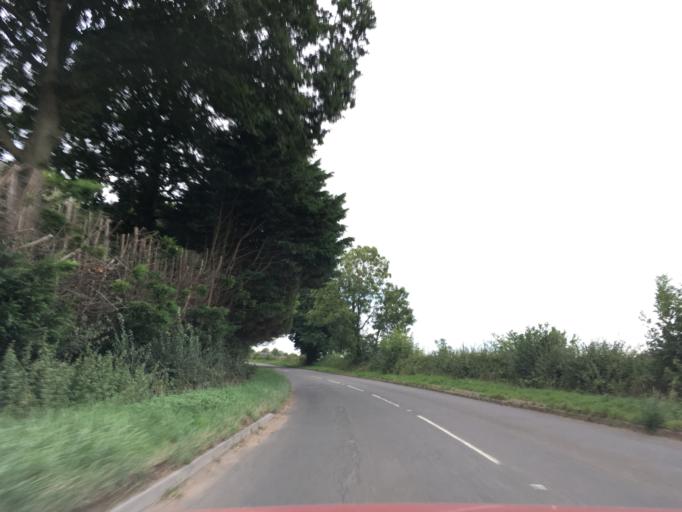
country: GB
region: England
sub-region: Wiltshire
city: Devizes
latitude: 51.3742
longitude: -2.0323
